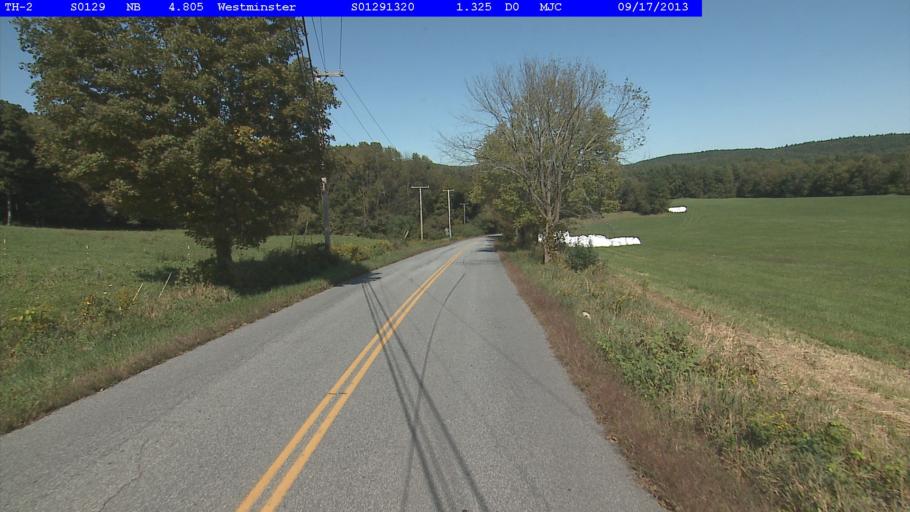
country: US
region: New Hampshire
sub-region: Cheshire County
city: Westmoreland
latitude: 43.0398
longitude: -72.5265
